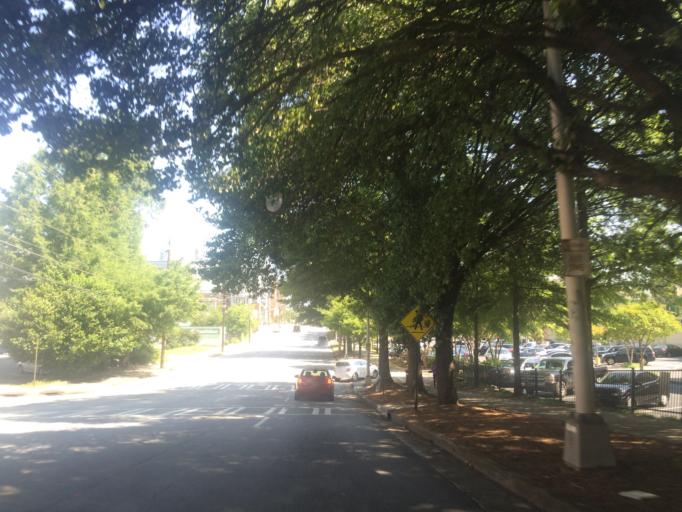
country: US
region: Georgia
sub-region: Fulton County
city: Atlanta
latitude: 33.7696
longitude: -84.3819
